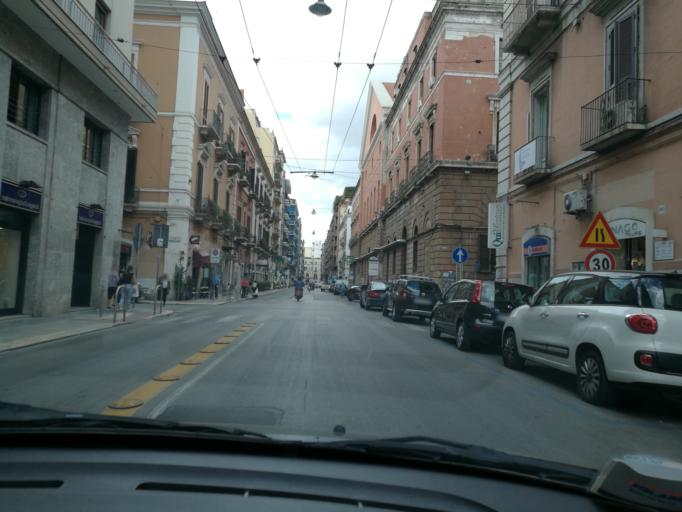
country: IT
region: Apulia
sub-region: Provincia di Bari
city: Bari
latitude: 41.1253
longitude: 16.8683
